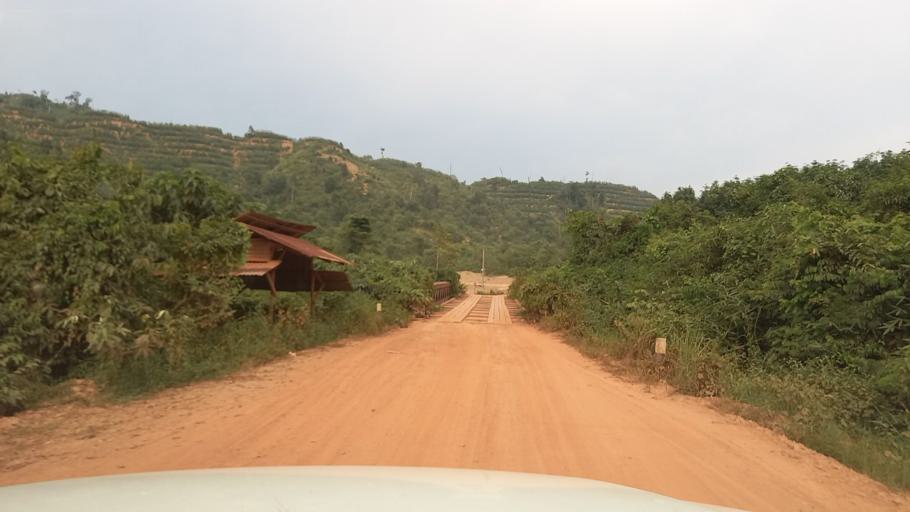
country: LA
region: Bolikhamxai
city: Bolikhan
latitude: 18.5177
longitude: 103.8336
